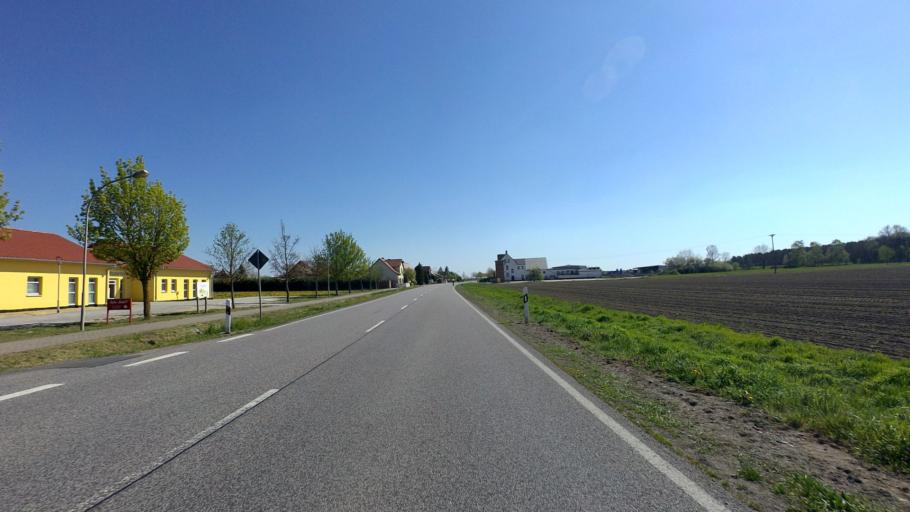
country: DE
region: Saxony-Anhalt
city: Pretzier
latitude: 52.7370
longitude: 11.2440
